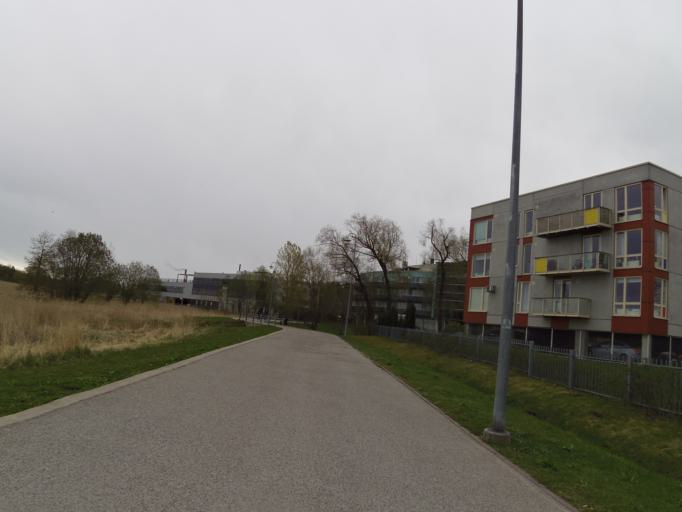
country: EE
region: Harju
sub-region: Saue vald
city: Laagri
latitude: 59.4286
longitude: 24.6614
